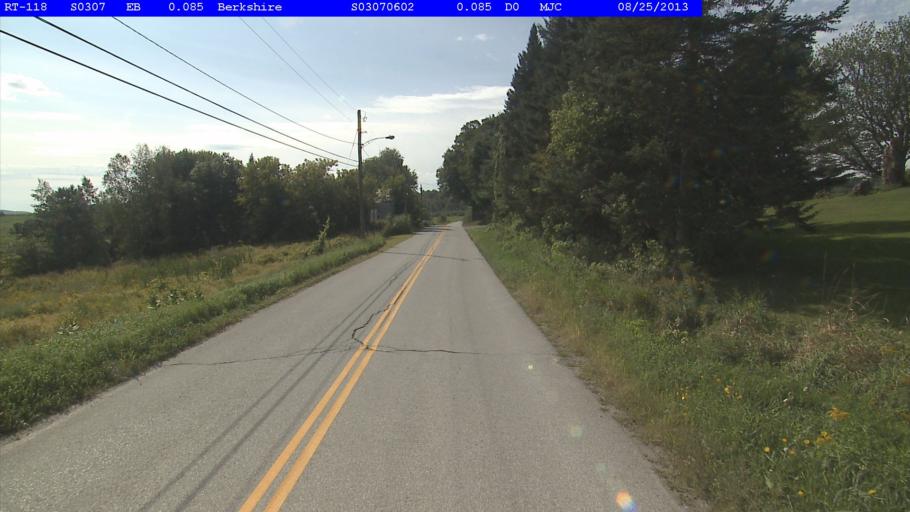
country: US
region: Vermont
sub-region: Franklin County
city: Richford
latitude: 44.9338
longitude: -72.7132
